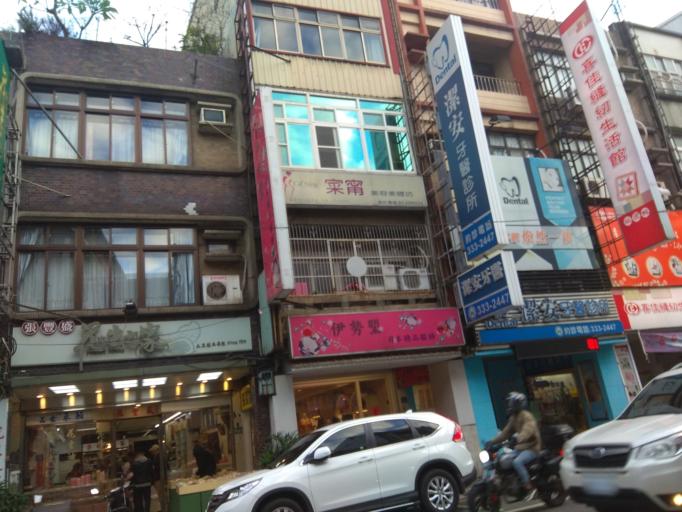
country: TW
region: Taiwan
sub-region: Taoyuan
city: Taoyuan
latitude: 24.9939
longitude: 121.3098
